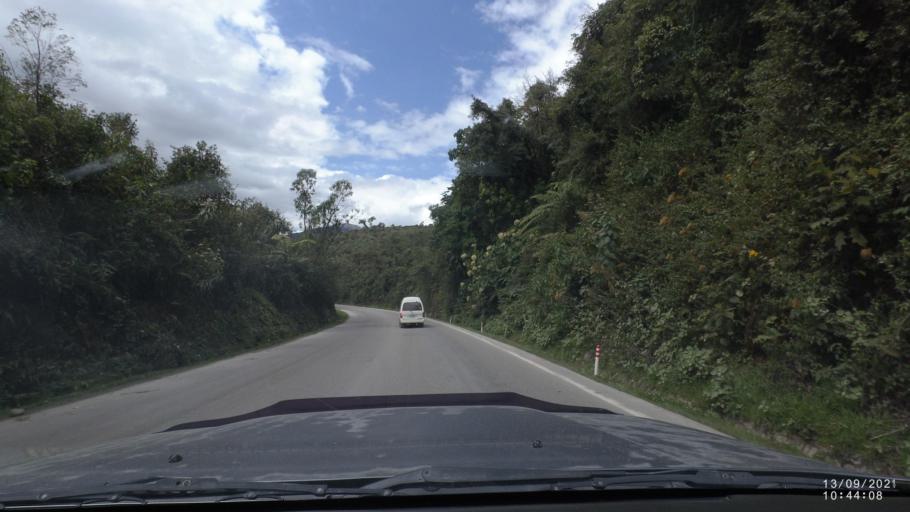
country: BO
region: Cochabamba
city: Colomi
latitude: -17.1913
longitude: -65.8821
